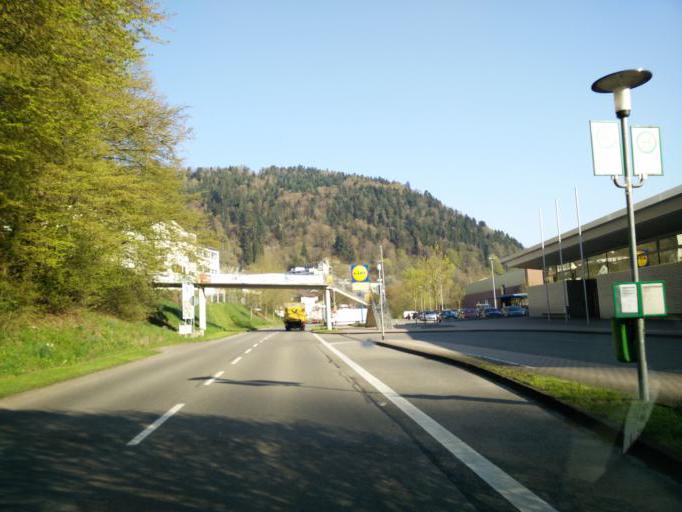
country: DE
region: Baden-Wuerttemberg
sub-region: Karlsruhe Region
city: Bad Liebenzell
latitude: 48.7752
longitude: 8.7327
